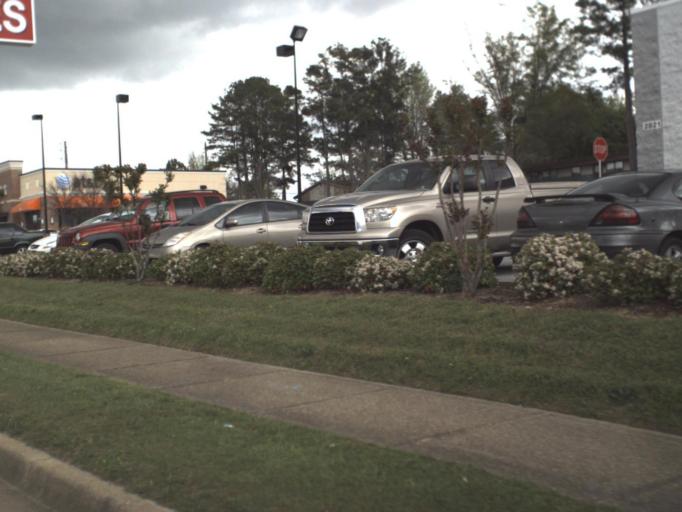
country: US
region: Florida
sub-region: Okaloosa County
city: Crestview
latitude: 30.7315
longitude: -86.5668
